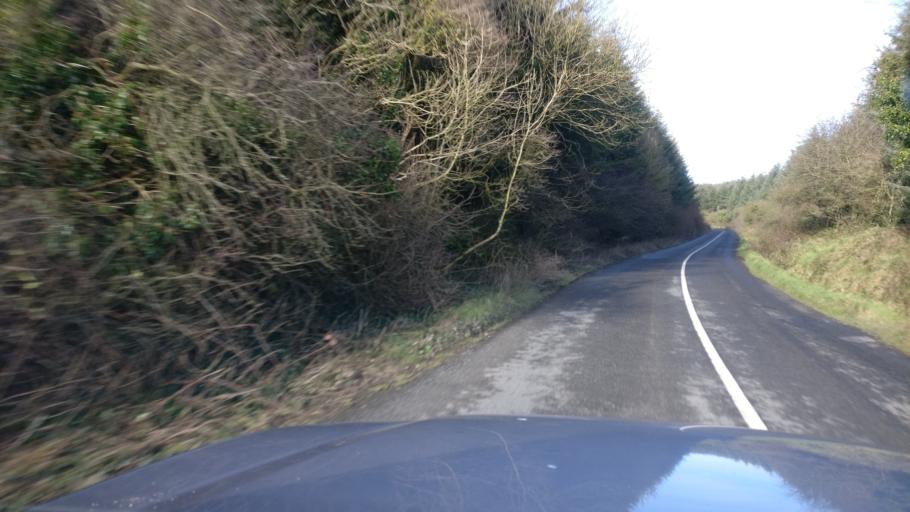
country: IE
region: Leinster
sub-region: Kilkenny
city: Castlecomer
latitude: 52.9109
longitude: -7.1834
